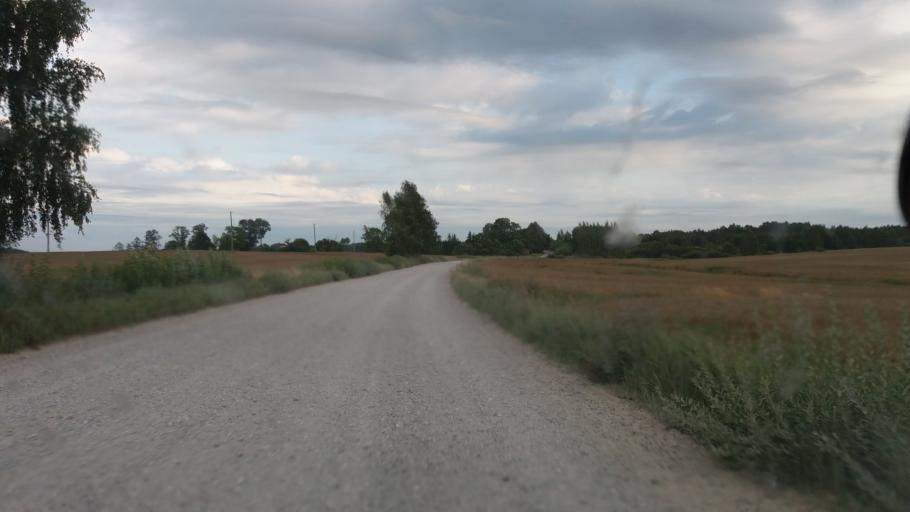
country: LV
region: Talsu Rajons
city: Sabile
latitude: 57.0301
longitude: 22.5793
